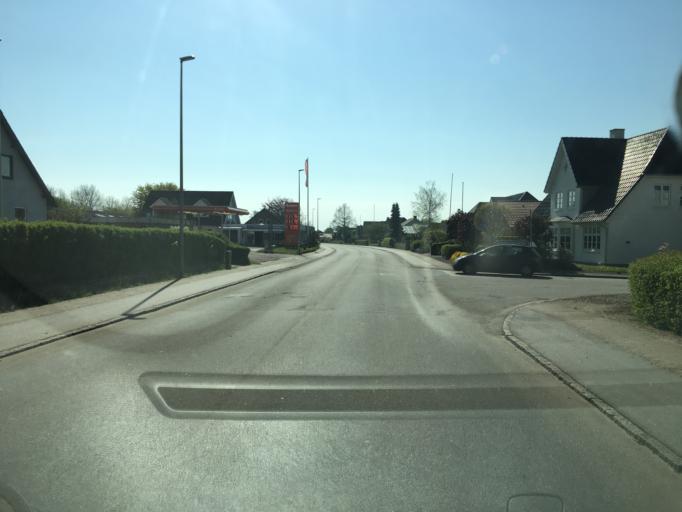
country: DK
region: South Denmark
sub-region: Haderslev Kommune
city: Vojens
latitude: 55.3195
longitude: 9.3010
